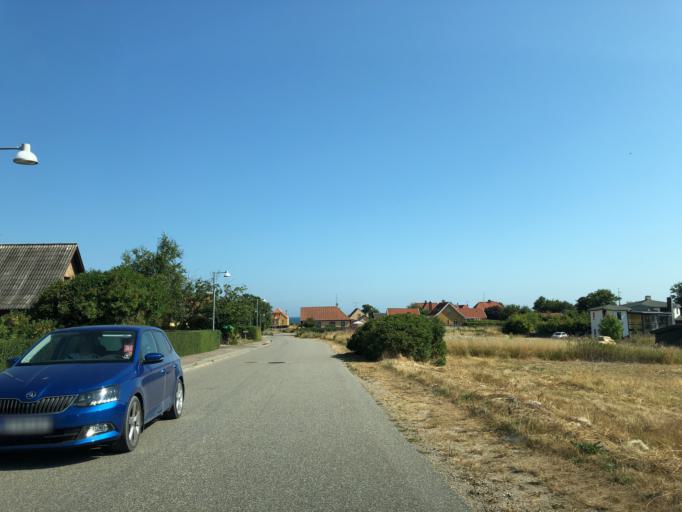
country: DK
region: Zealand
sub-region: Odsherred Kommune
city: Asnaes
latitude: 55.9715
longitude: 11.3593
